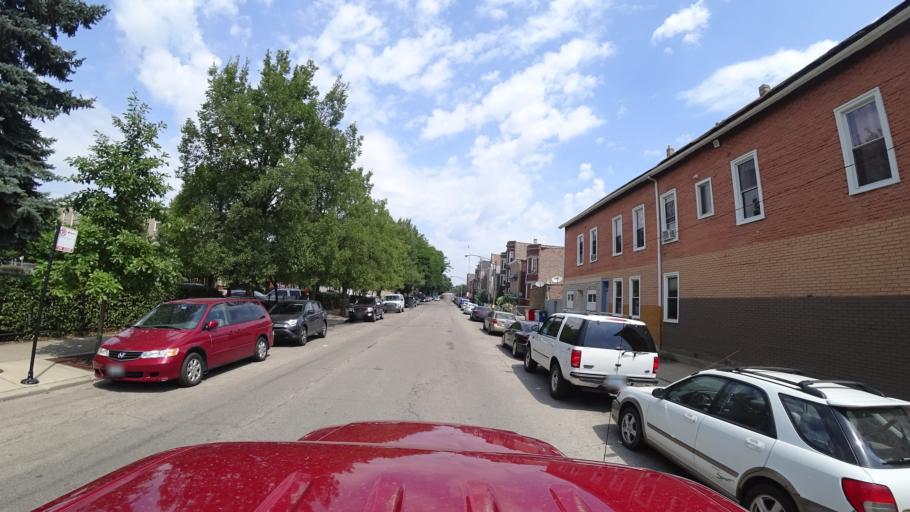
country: US
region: Illinois
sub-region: Cook County
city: Chicago
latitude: 41.8348
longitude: -87.6486
